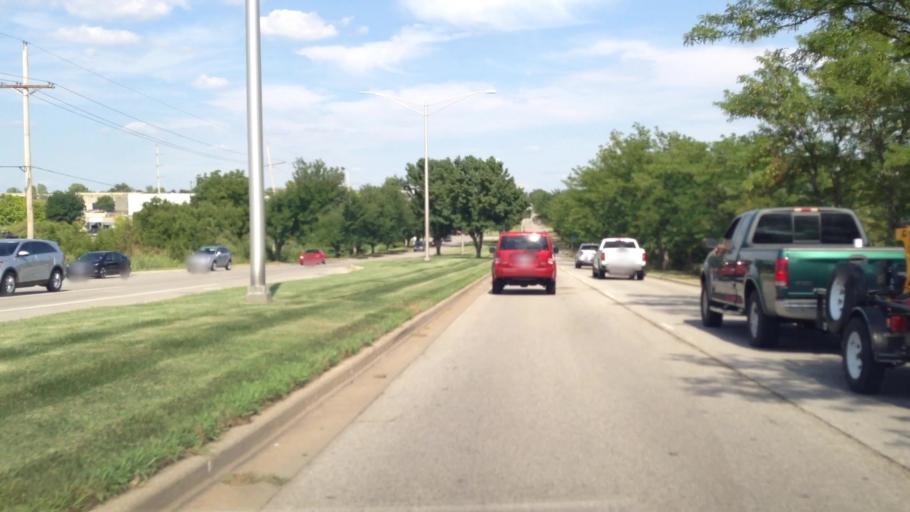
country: US
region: Kansas
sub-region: Johnson County
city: Lenexa
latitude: 38.9273
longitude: -94.7787
